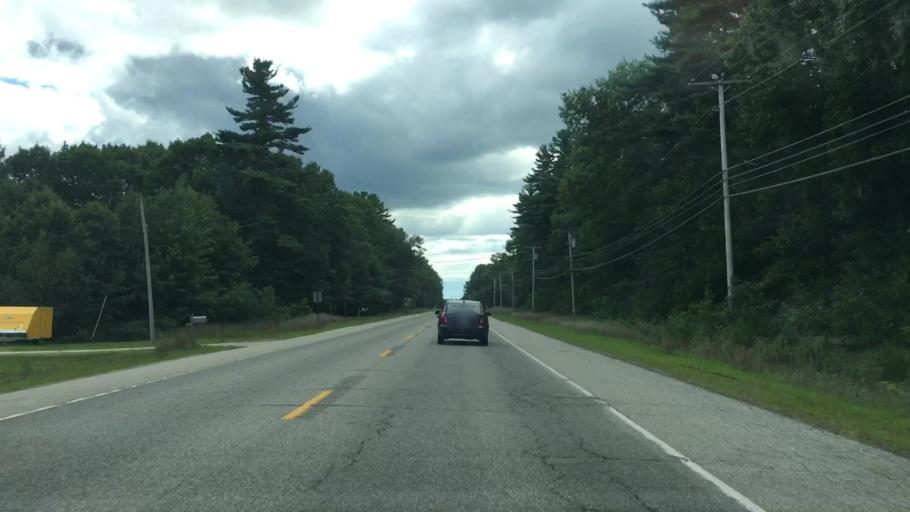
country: US
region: Maine
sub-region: York County
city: North Berwick
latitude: 43.3339
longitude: -70.7345
